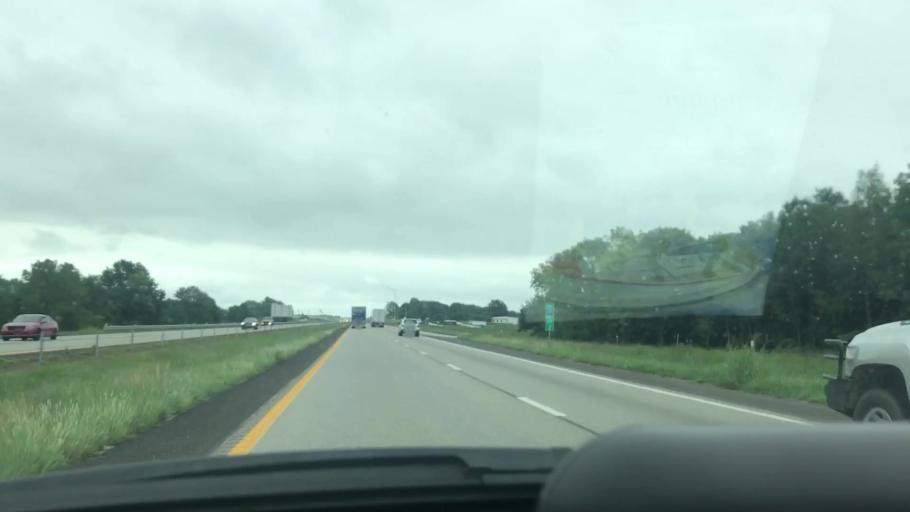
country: US
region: Missouri
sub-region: Greene County
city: Republic
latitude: 37.1967
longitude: -93.4412
